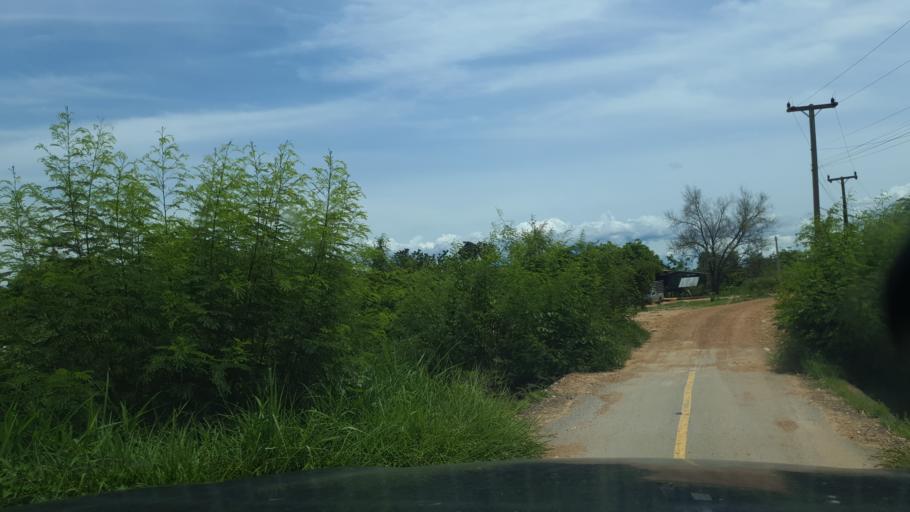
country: TH
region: Sukhothai
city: Ban Na
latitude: 17.1289
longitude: 99.6721
